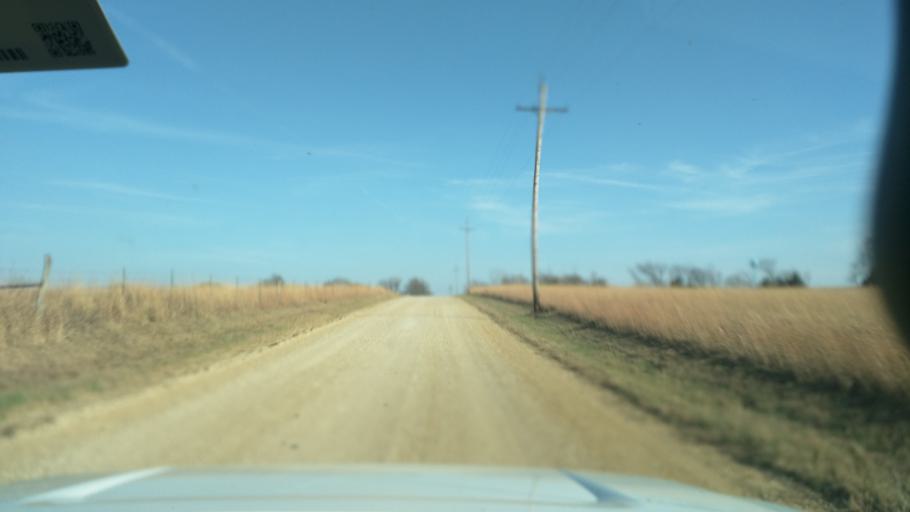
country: US
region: Kansas
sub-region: Lyon County
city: Emporia
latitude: 38.2890
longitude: -96.1780
